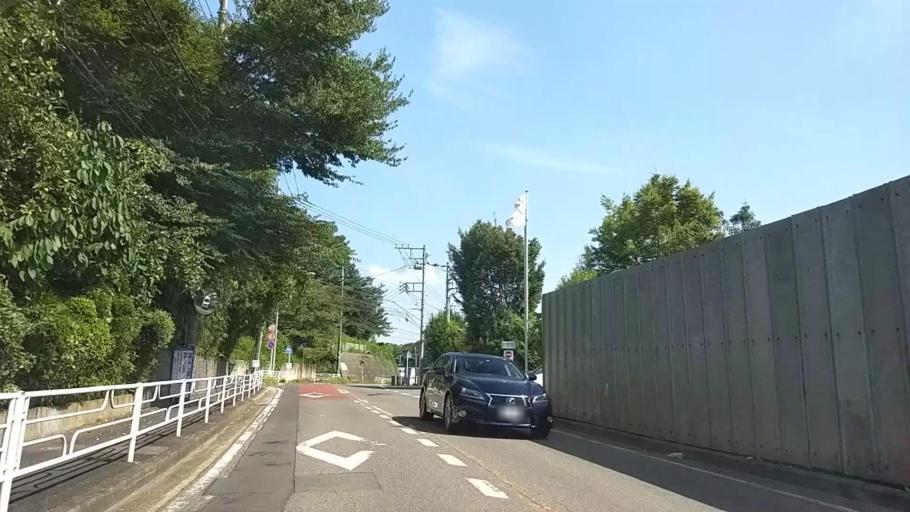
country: JP
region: Kanagawa
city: Yokohama
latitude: 35.5269
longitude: 139.5764
